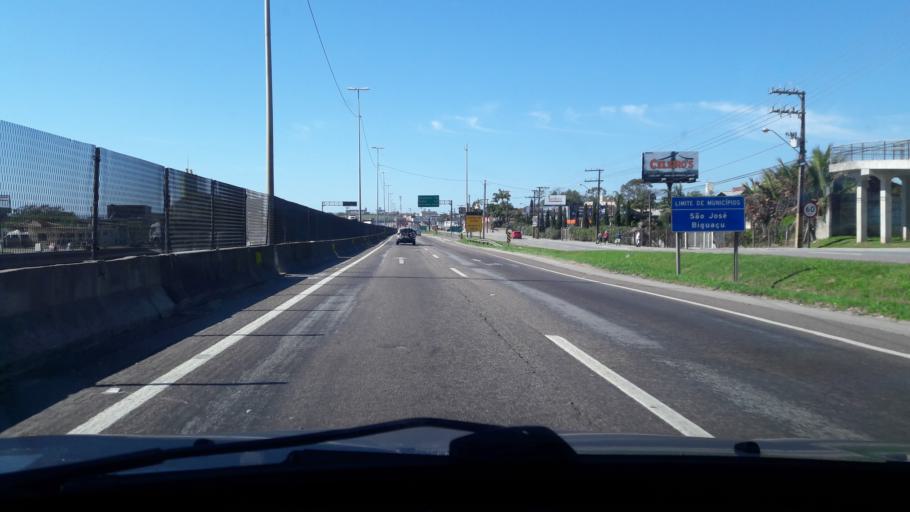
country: BR
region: Santa Catarina
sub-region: Biguacu
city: Biguacu
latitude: -27.5291
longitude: -48.6334
